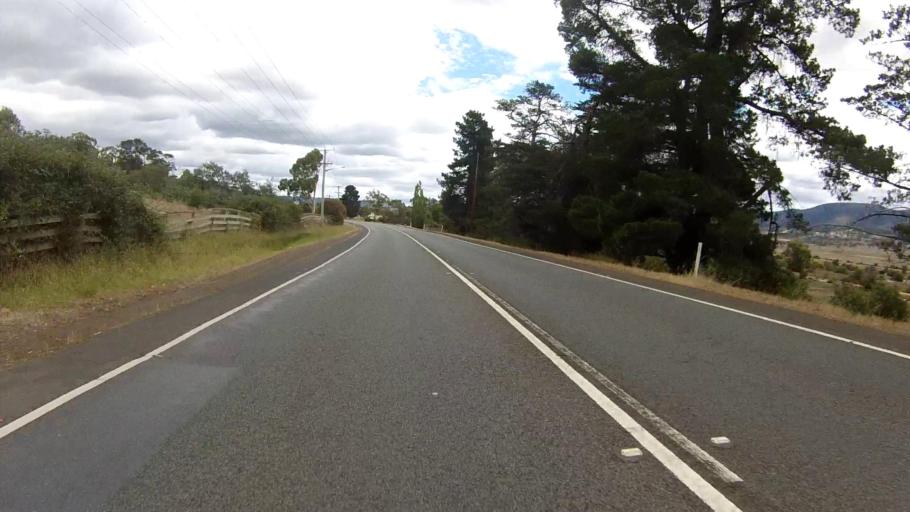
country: AU
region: Tasmania
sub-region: Brighton
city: Bridgewater
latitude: -42.6793
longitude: 147.2654
